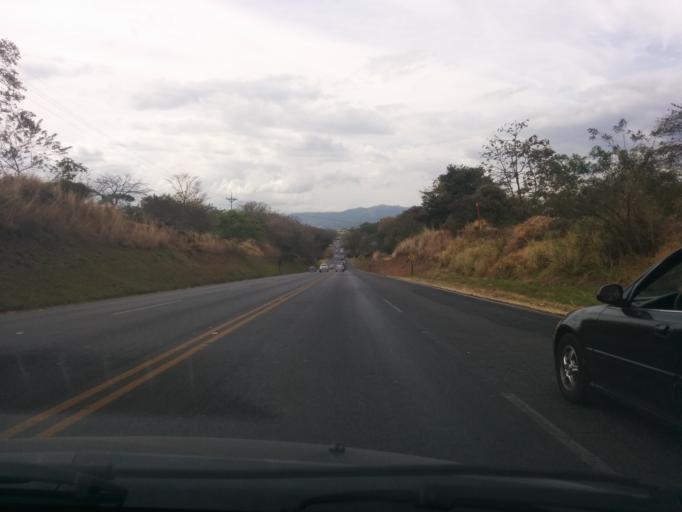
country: CR
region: Alajuela
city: Carrillos
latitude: 10.0016
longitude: -84.2842
